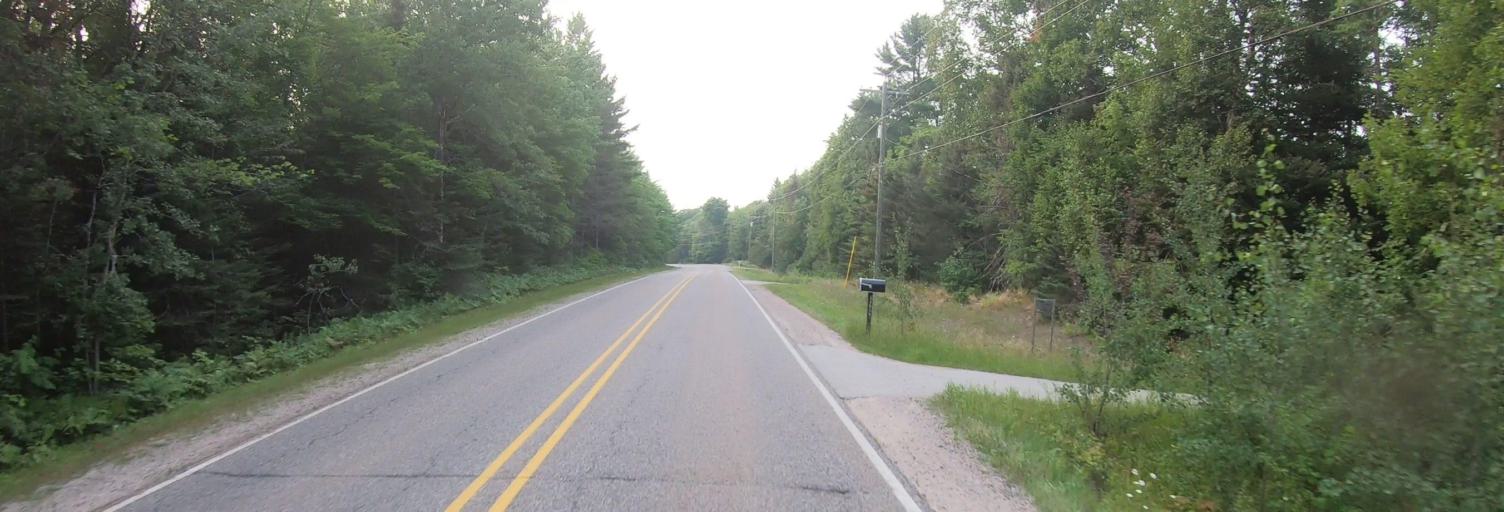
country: US
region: Michigan
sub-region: Chippewa County
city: Sault Ste. Marie
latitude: 46.4815
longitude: -84.6280
